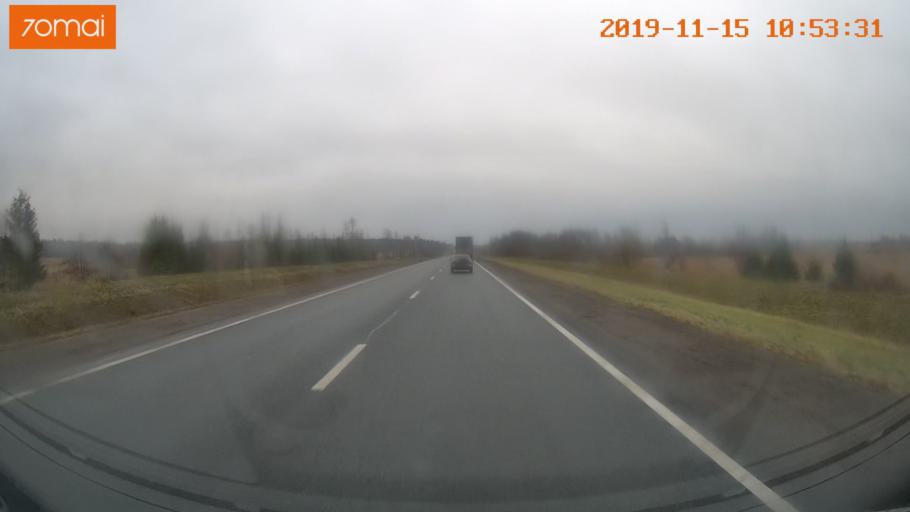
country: RU
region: Vologda
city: Chebsara
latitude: 59.1688
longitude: 38.7563
